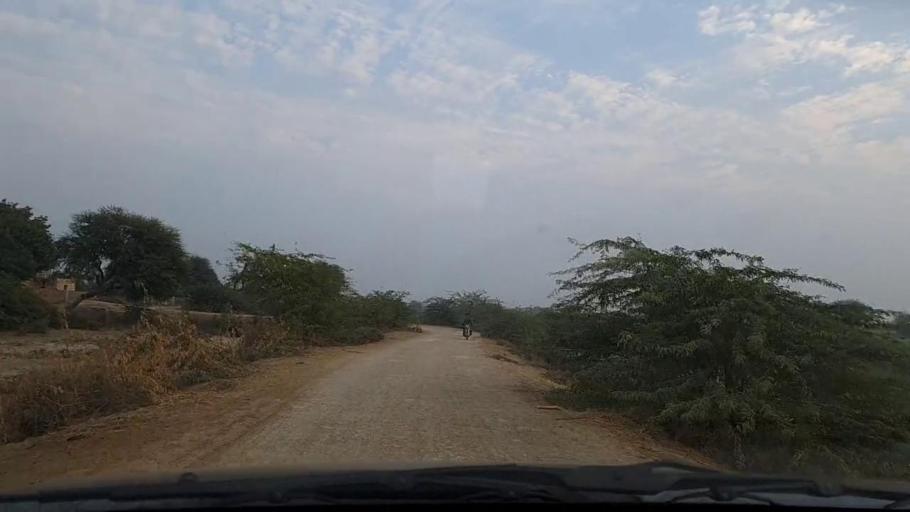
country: PK
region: Sindh
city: Pithoro
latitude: 25.5986
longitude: 69.4607
